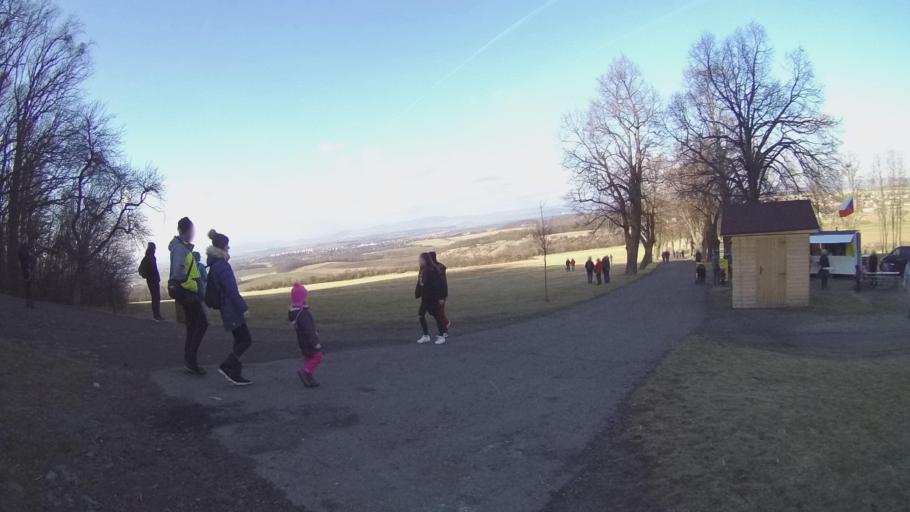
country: CZ
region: Ustecky
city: Roudnice nad Labem
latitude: 50.3910
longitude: 14.2908
